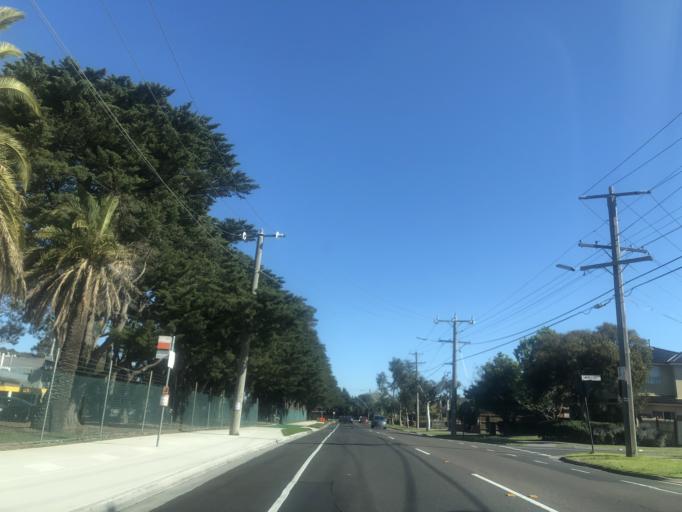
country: AU
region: Victoria
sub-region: Monash
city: Clayton
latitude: -37.9053
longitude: 145.1282
